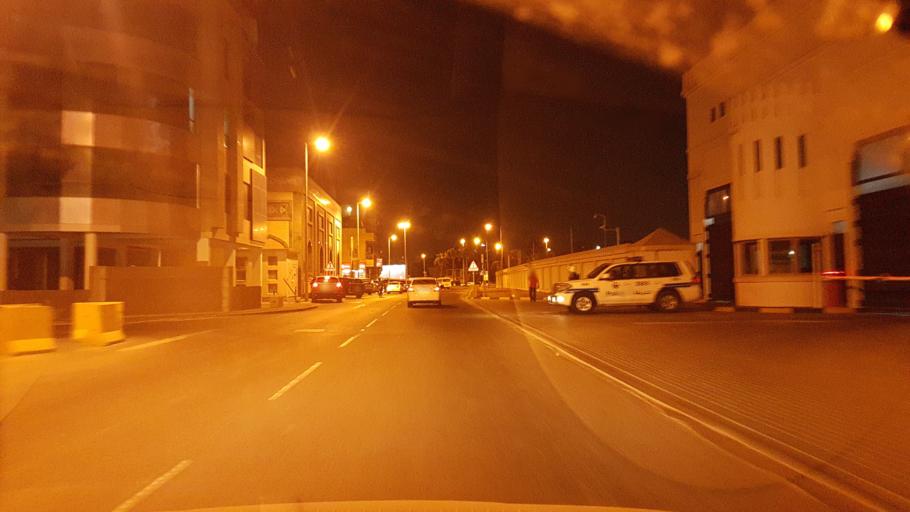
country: BH
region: Manama
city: Manama
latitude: 26.2213
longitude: 50.5781
